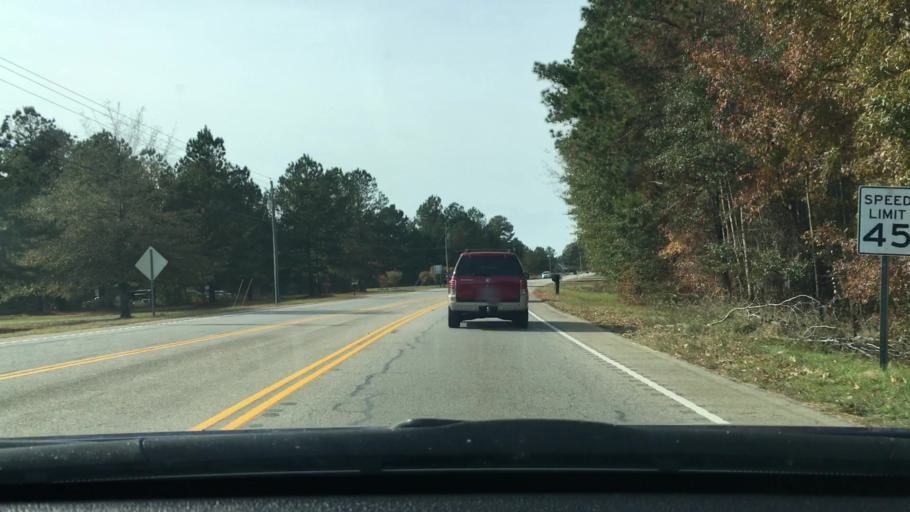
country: US
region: South Carolina
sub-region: Sumter County
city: Cherryvale
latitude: 33.9364
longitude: -80.4549
